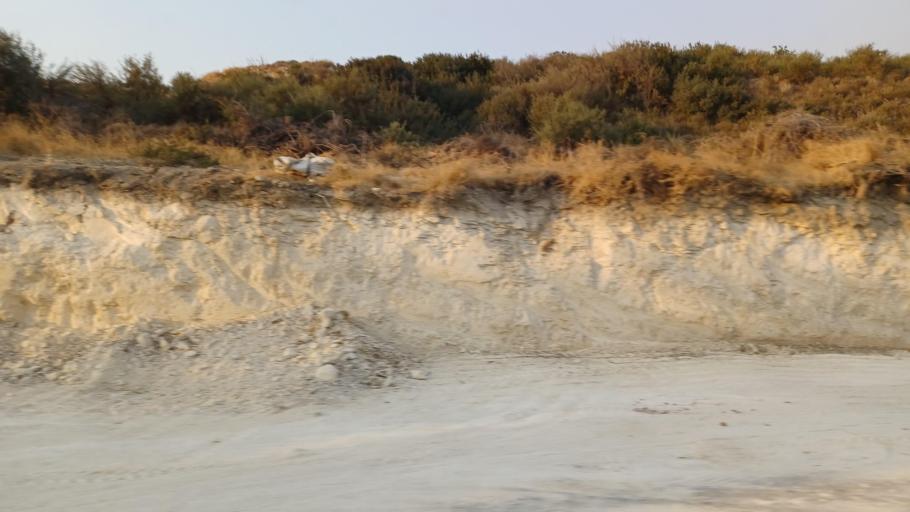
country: CY
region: Limassol
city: Pissouri
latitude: 34.6832
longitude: 32.6932
